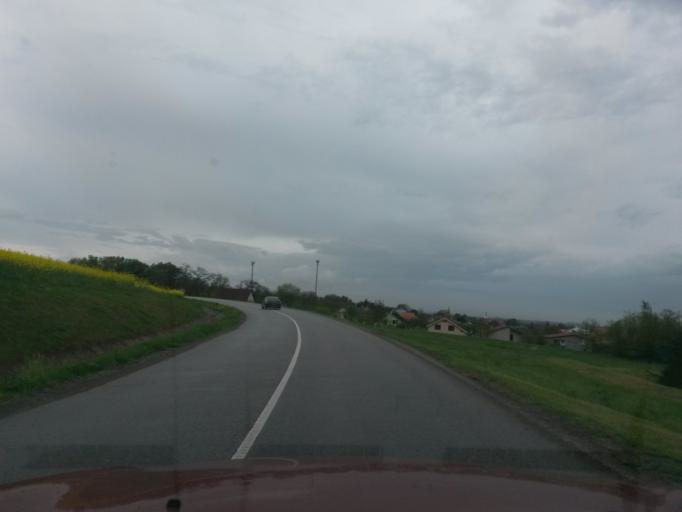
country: HU
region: Borsod-Abauj-Zemplen
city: Gonc
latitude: 48.5506
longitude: 21.2588
